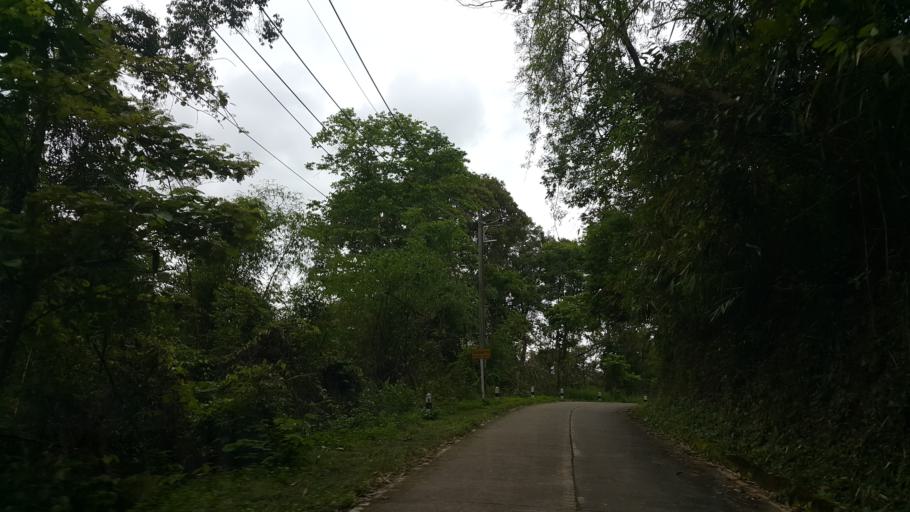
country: TH
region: Lampang
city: Mueang Pan
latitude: 18.8246
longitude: 99.4255
